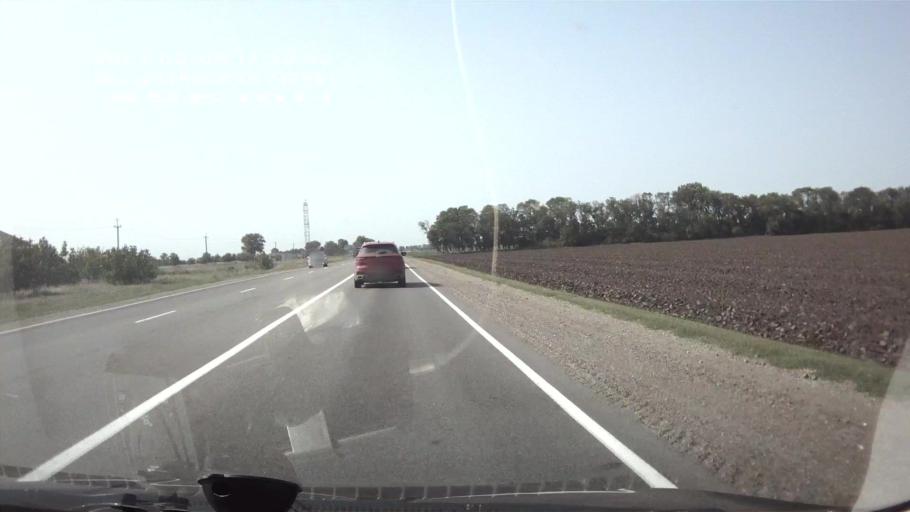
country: RU
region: Krasnodarskiy
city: Ust'-Labinsk
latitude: 45.2439
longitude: 39.7110
